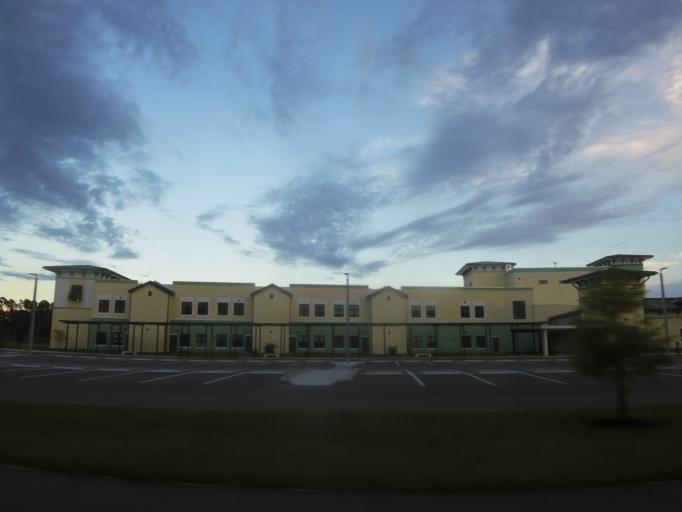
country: US
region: Florida
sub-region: Saint Johns County
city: Palm Valley
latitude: 30.1213
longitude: -81.4083
